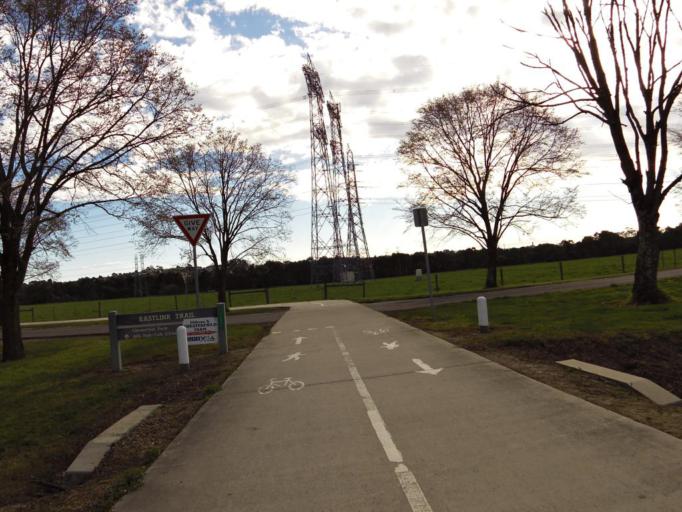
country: AU
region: Victoria
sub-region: Monash
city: Mulgrave
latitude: -37.9051
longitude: 145.2099
